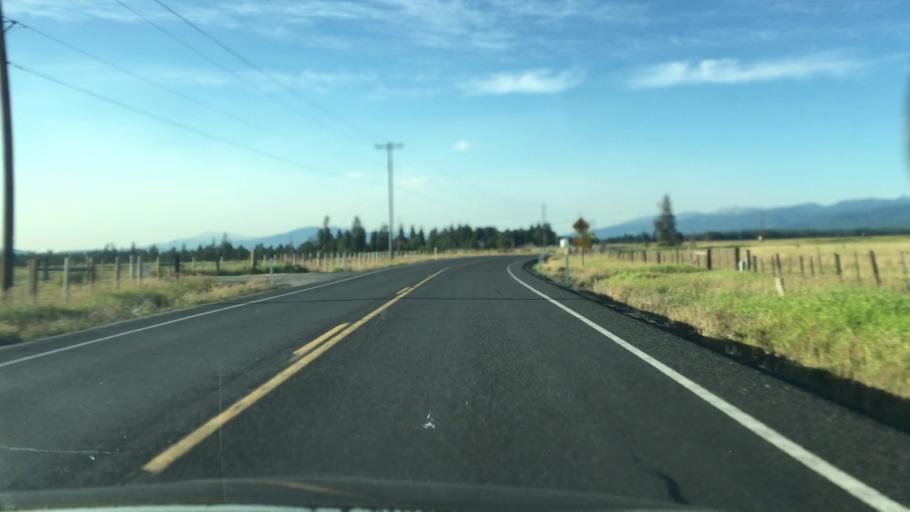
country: US
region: Idaho
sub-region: Valley County
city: McCall
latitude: 44.7708
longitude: -116.0782
